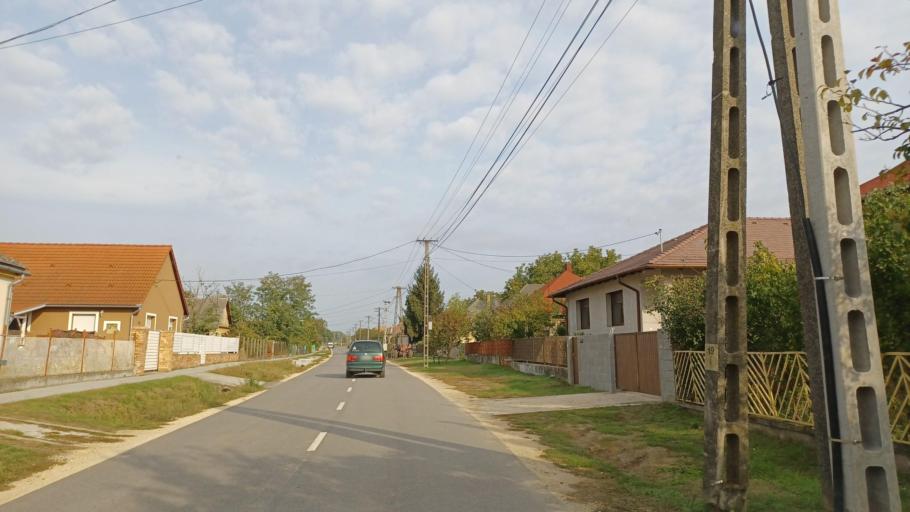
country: HU
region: Tolna
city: Nagydorog
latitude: 46.5978
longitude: 18.7183
